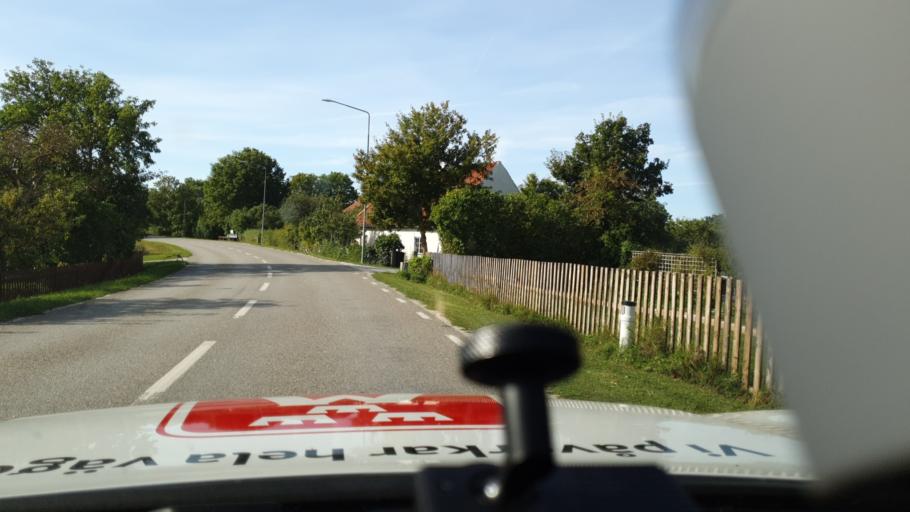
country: SE
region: Gotland
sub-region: Gotland
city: Slite
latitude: 57.8482
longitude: 18.7827
